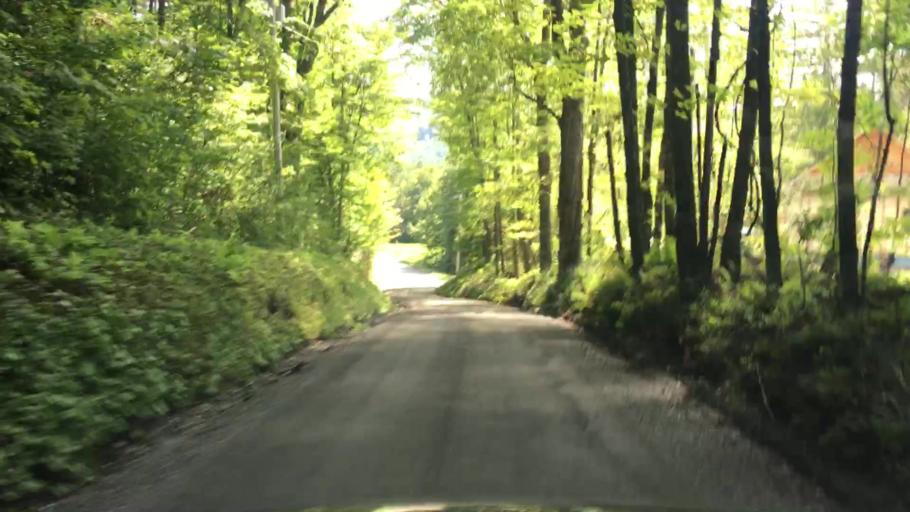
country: US
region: Vermont
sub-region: Windham County
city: West Brattleboro
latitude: 42.7955
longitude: -72.6337
